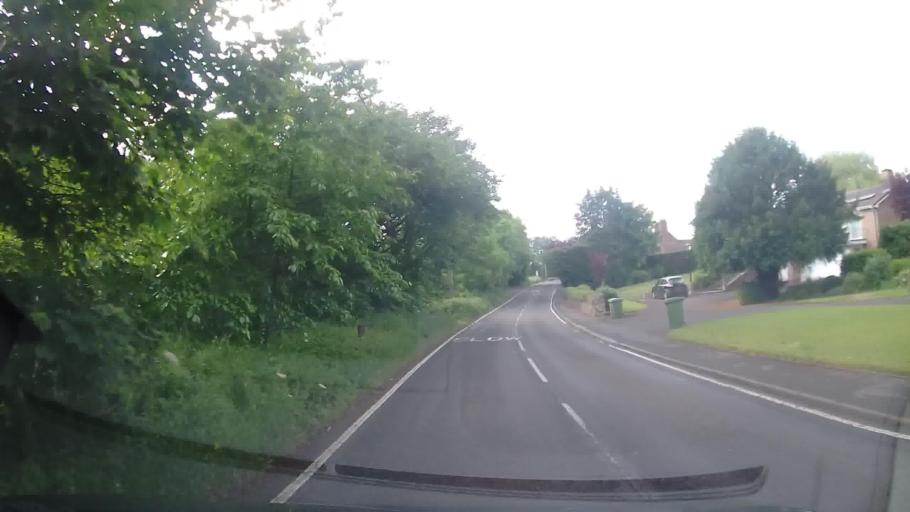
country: GB
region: England
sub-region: Shropshire
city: Harley
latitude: 52.6449
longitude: -2.5757
